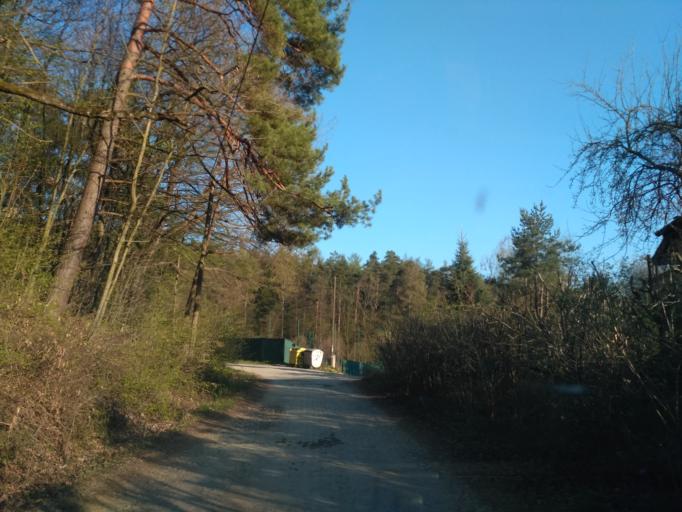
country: SK
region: Kosicky
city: Kosice
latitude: 48.7333
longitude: 21.1610
